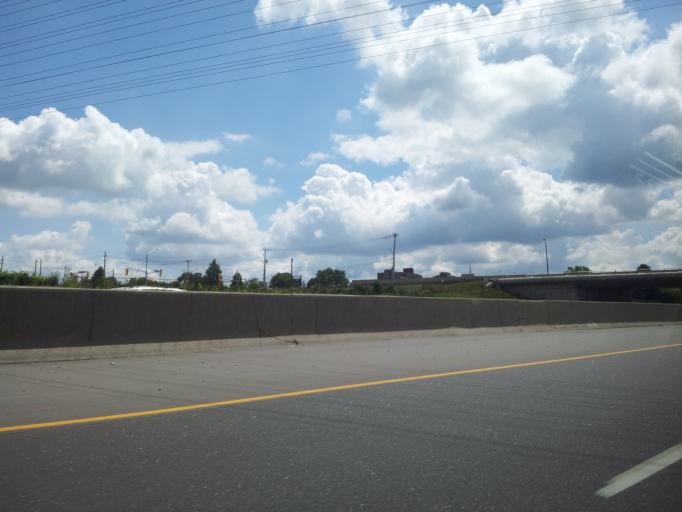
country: CA
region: Ontario
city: Waterloo
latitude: 43.4631
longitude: -80.4712
